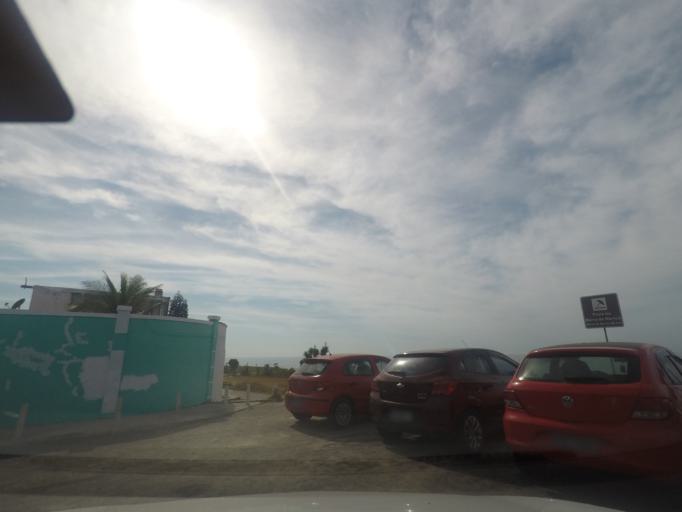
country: BR
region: Rio de Janeiro
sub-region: Marica
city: Marica
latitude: -22.9615
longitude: -42.8276
